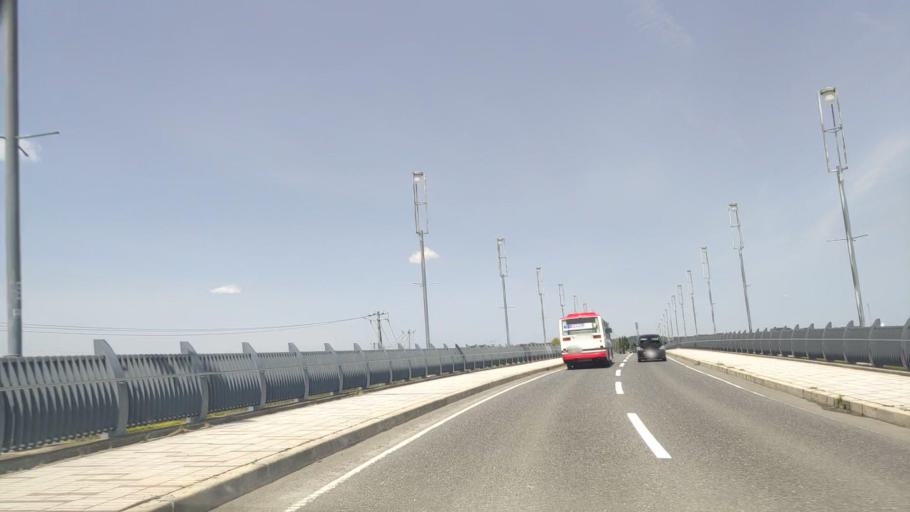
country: JP
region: Aomori
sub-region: Hachinohe Shi
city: Uchimaru
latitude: 40.4999
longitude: 141.4440
